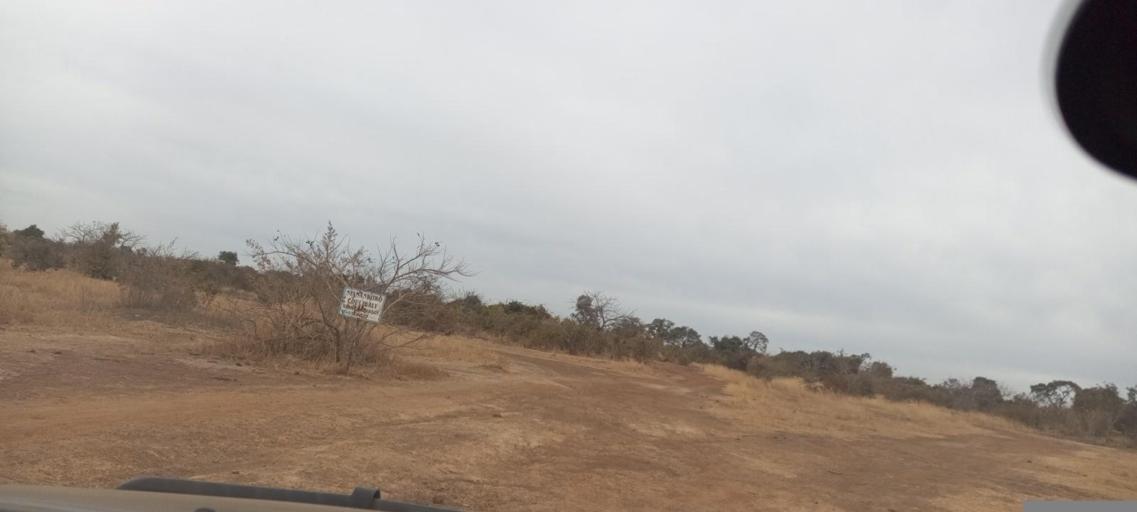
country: ML
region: Koulikoro
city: Kati
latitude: 12.7607
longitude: -8.2840
